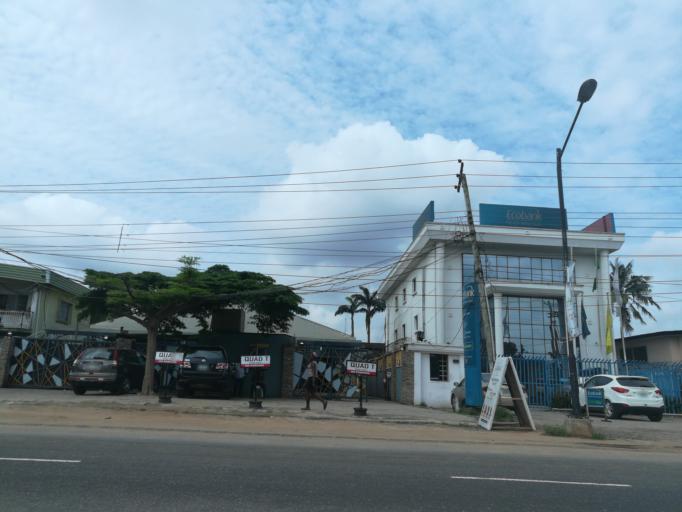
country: NG
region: Lagos
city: Somolu
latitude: 6.5505
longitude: 3.3765
